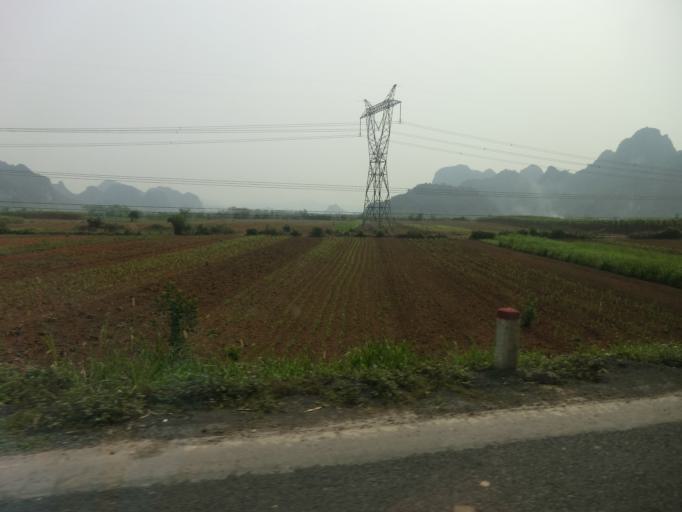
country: VN
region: Hoa Binh
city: Thi Tran Hang Tram
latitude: 20.4143
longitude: 105.6221
